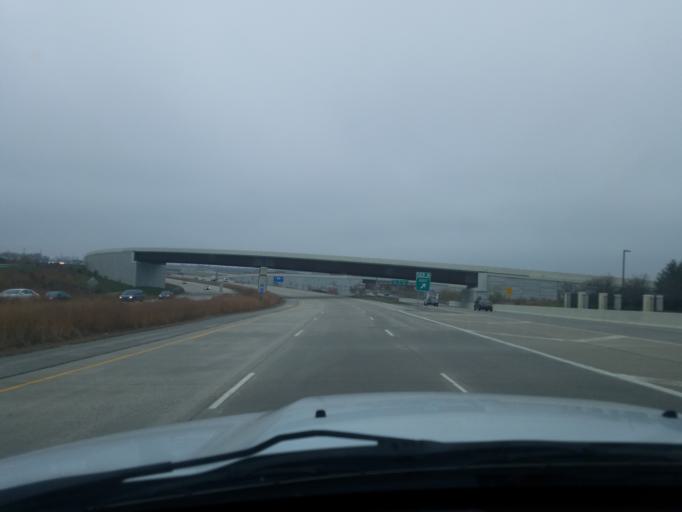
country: US
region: Indiana
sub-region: Hamilton County
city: Carmel
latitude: 39.9943
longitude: -86.1265
